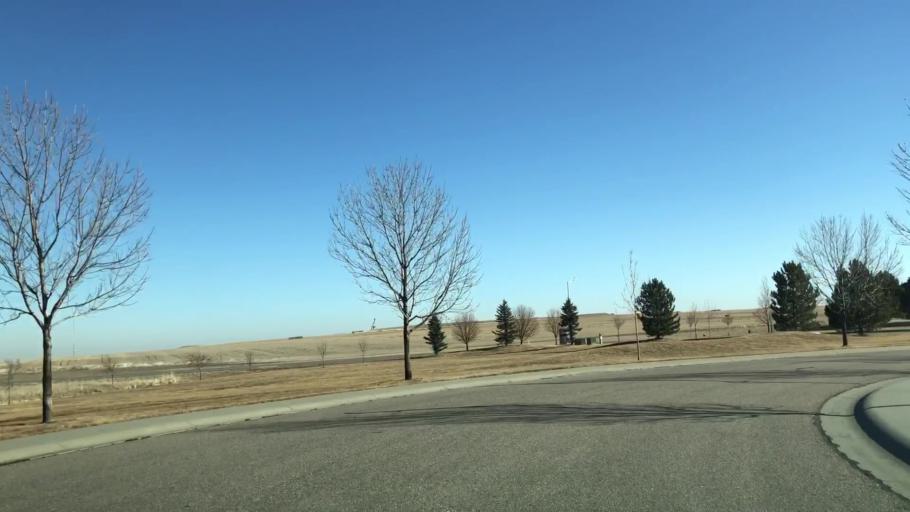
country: US
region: Colorado
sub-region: Weld County
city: Windsor
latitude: 40.4553
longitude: -104.9456
